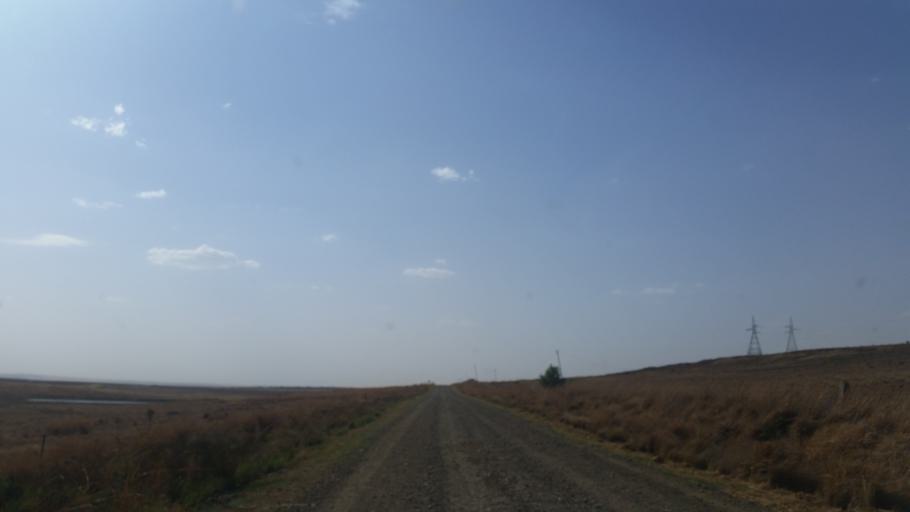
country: ZA
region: Orange Free State
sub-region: Thabo Mofutsanyana District Municipality
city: Phuthaditjhaba
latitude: -28.2814
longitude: 28.6443
